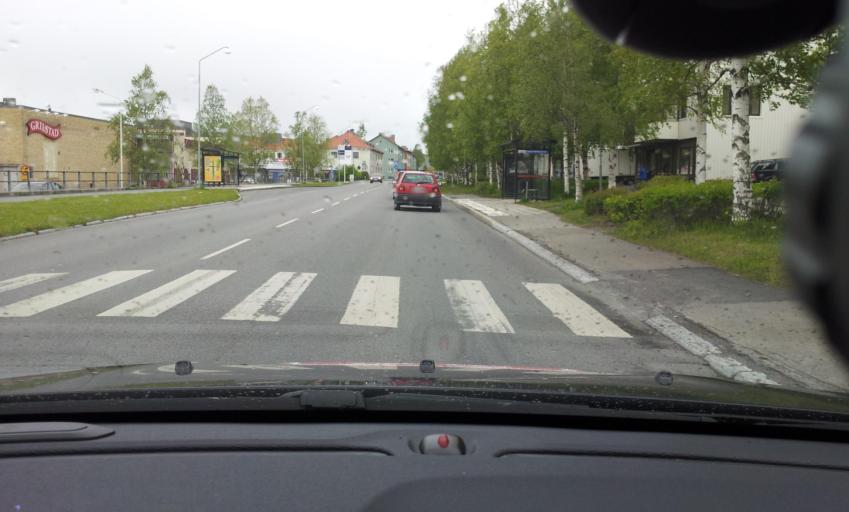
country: SE
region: Jaemtland
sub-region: OEstersunds Kommun
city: Ostersund
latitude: 63.1676
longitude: 14.6477
